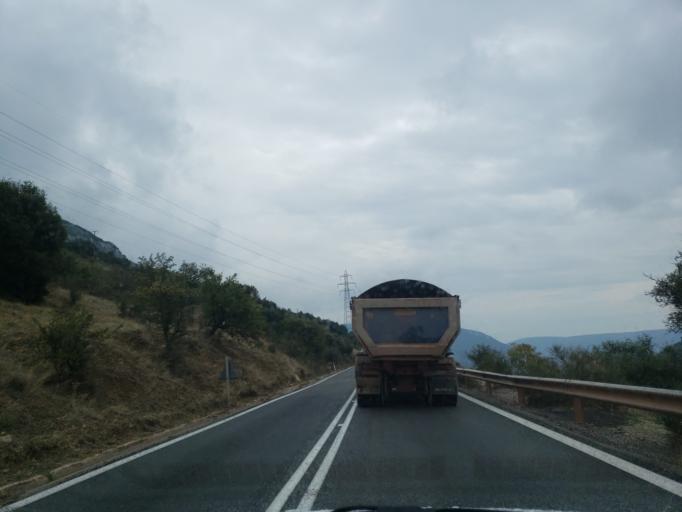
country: GR
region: Central Greece
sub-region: Nomos Fokidos
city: Amfissa
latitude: 38.5686
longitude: 22.3981
